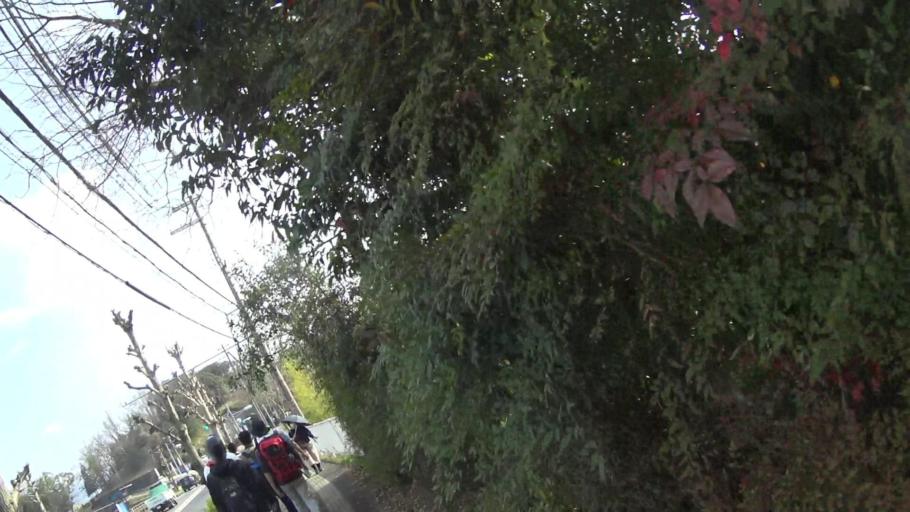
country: JP
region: Nara
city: Nara-shi
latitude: 34.6954
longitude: 135.8255
